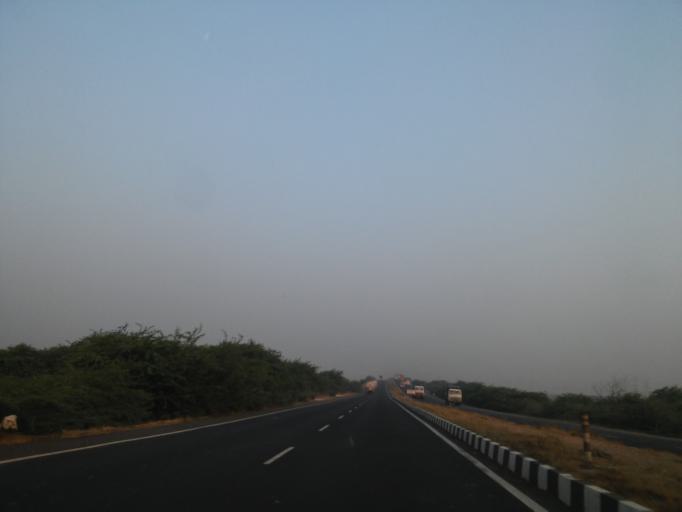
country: IN
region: Gujarat
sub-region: Rajkot
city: Morbi
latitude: 23.1237
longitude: 70.7654
